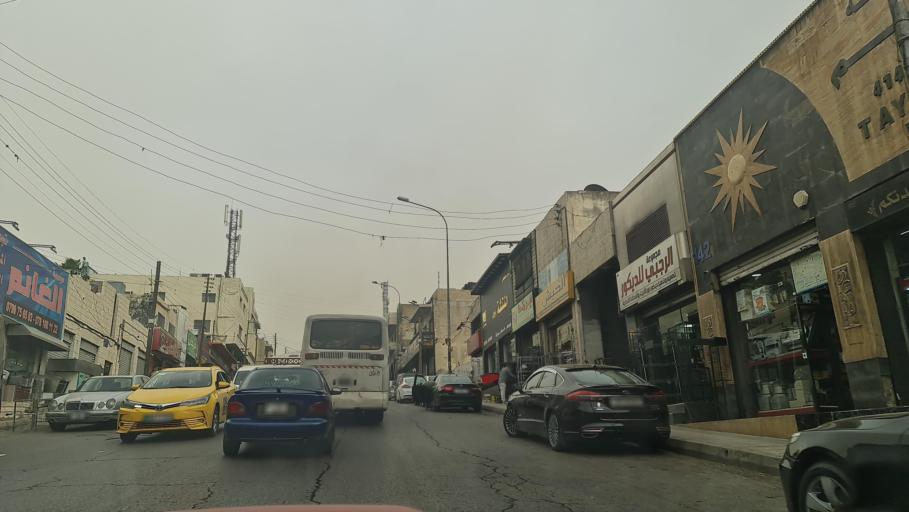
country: JO
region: Amman
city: Amman
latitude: 31.9353
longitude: 35.9318
